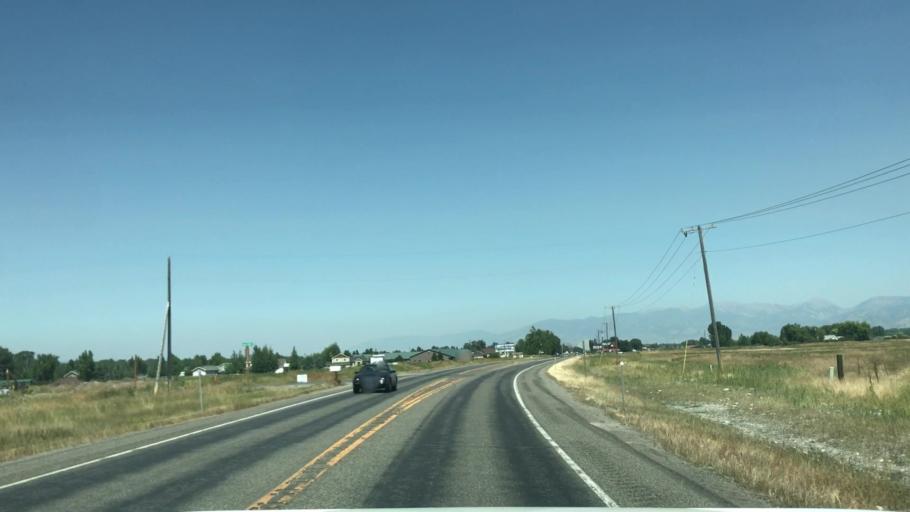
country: US
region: Montana
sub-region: Gallatin County
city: Four Corners
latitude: 45.6423
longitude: -111.1961
